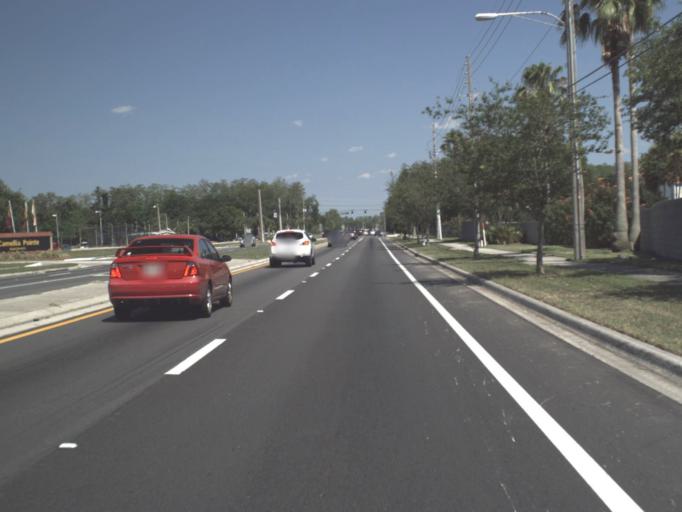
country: US
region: Florida
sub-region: Orange County
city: Azalea Park
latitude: 28.5191
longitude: -81.2987
